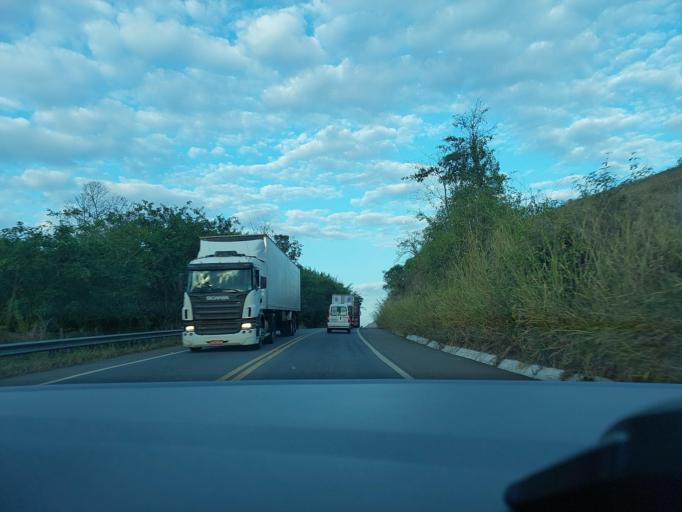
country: BR
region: Rio de Janeiro
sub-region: Natividade
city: Natividade
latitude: -21.1493
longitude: -42.1513
